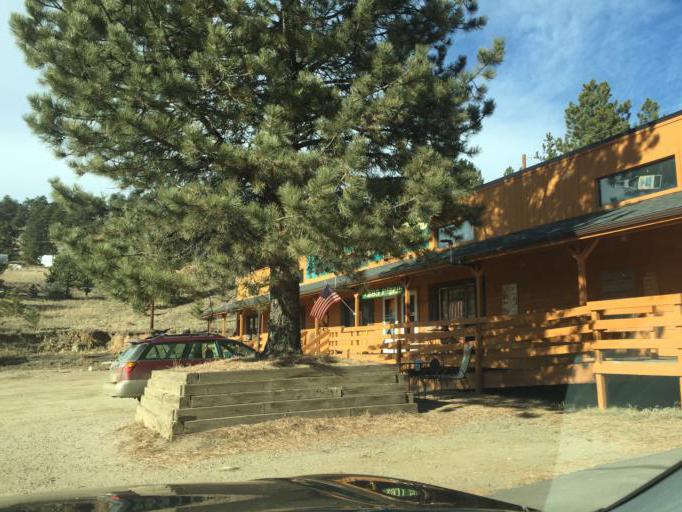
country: US
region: Colorado
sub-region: Jefferson County
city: Evergreen
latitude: 39.4377
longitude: -105.4604
